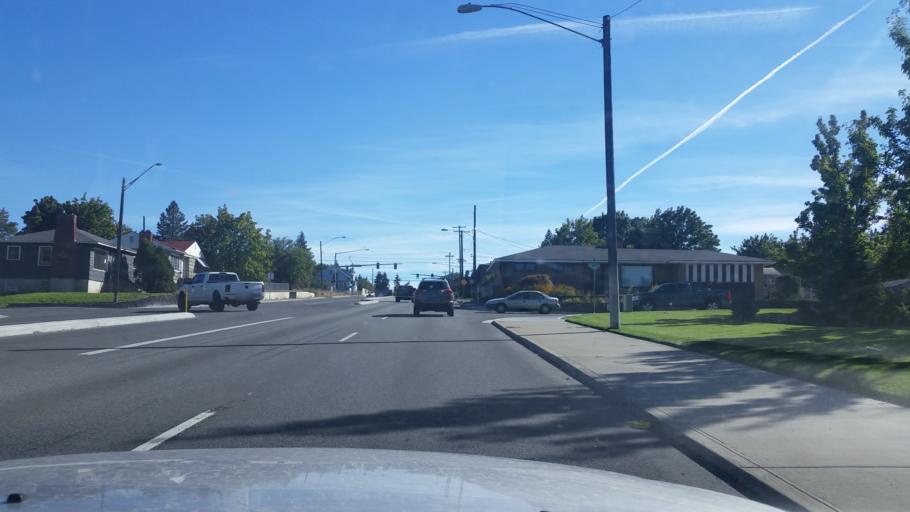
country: US
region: Washington
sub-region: Spokane County
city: Spokane
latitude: 47.6297
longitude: -117.3633
